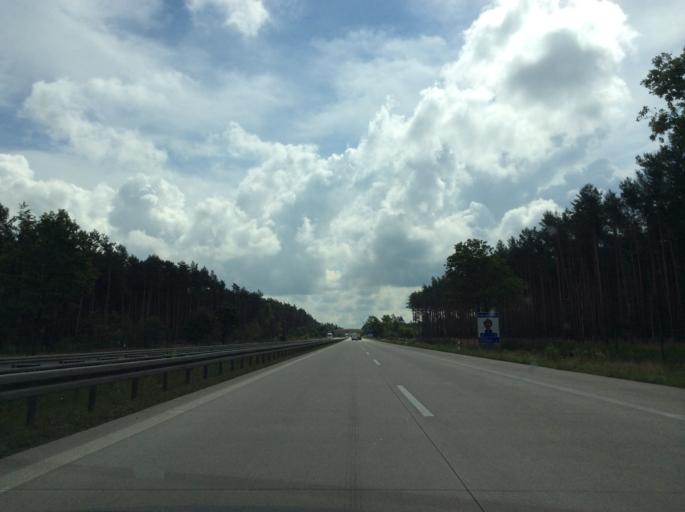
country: DE
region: Brandenburg
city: Briesen
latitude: 52.3239
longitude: 14.3012
